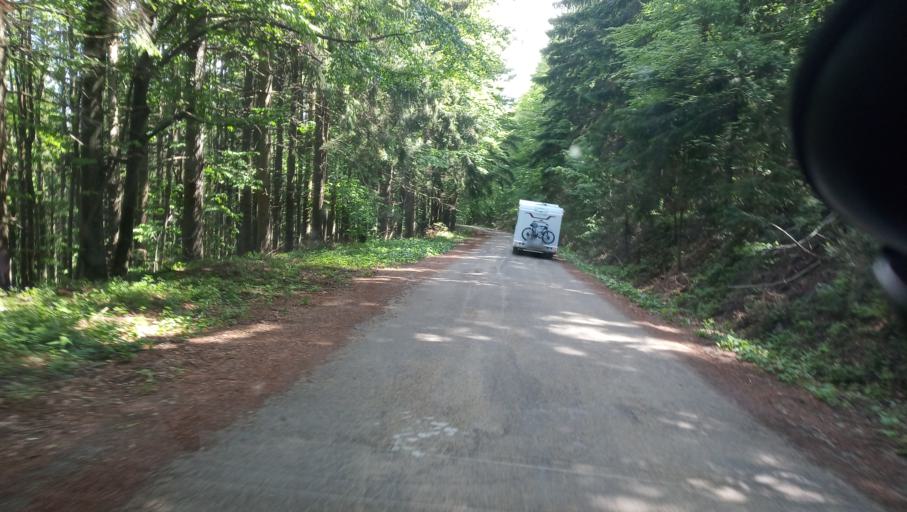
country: RO
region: Caras-Severin
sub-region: Comuna Valiug
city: Valiug
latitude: 45.2156
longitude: 22.0608
